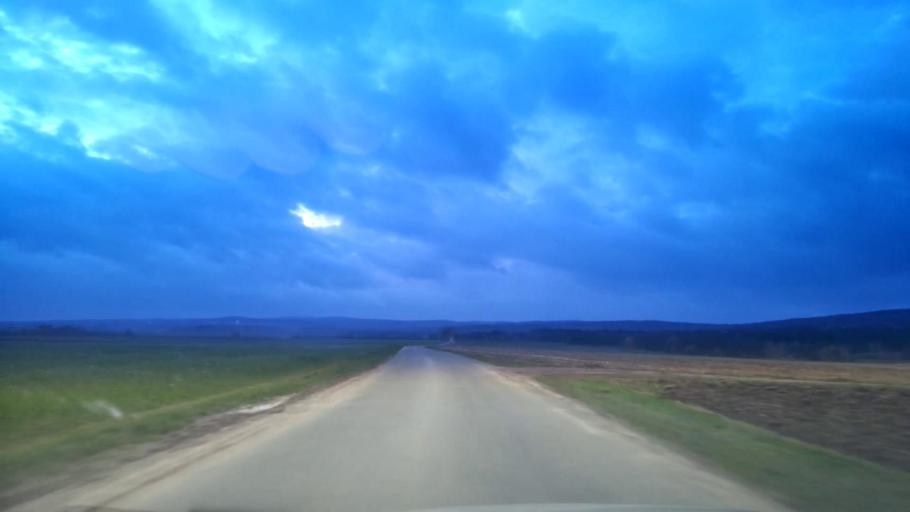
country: DE
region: Bavaria
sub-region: Upper Palatinate
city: Wiesau
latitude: 49.9429
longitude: 12.1990
